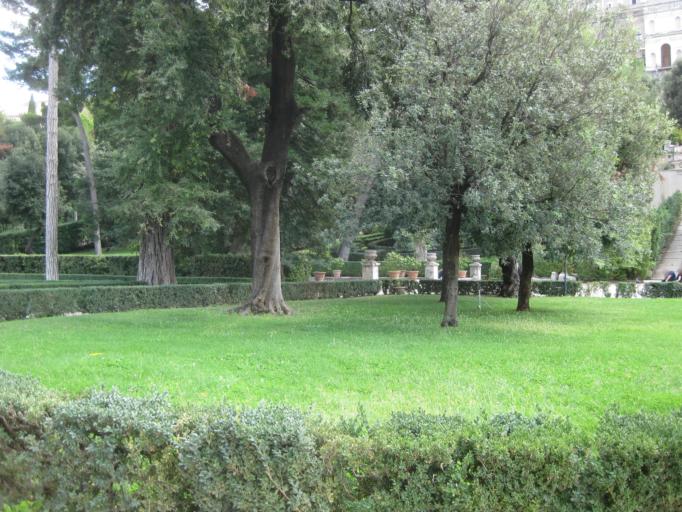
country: IT
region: Latium
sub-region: Citta metropolitana di Roma Capitale
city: Tivoli
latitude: 41.9632
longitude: 12.7944
